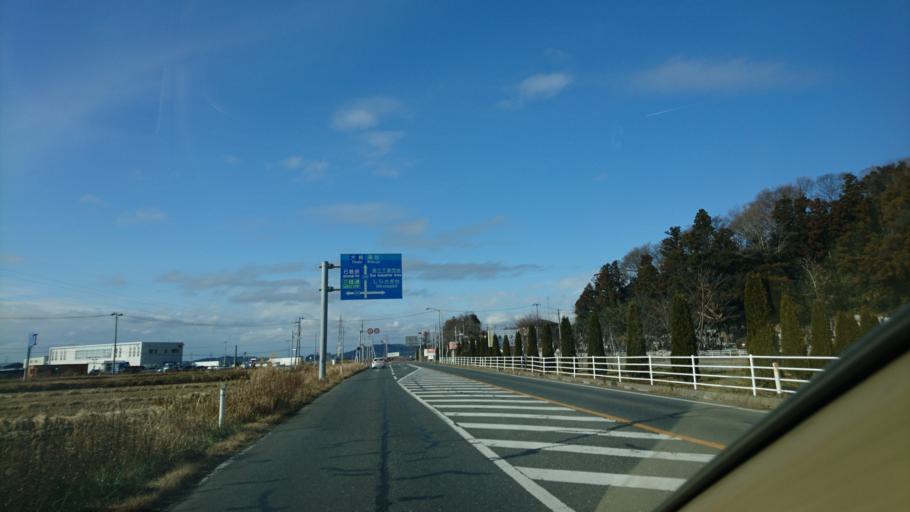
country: JP
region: Miyagi
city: Yamoto
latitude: 38.4594
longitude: 141.2458
